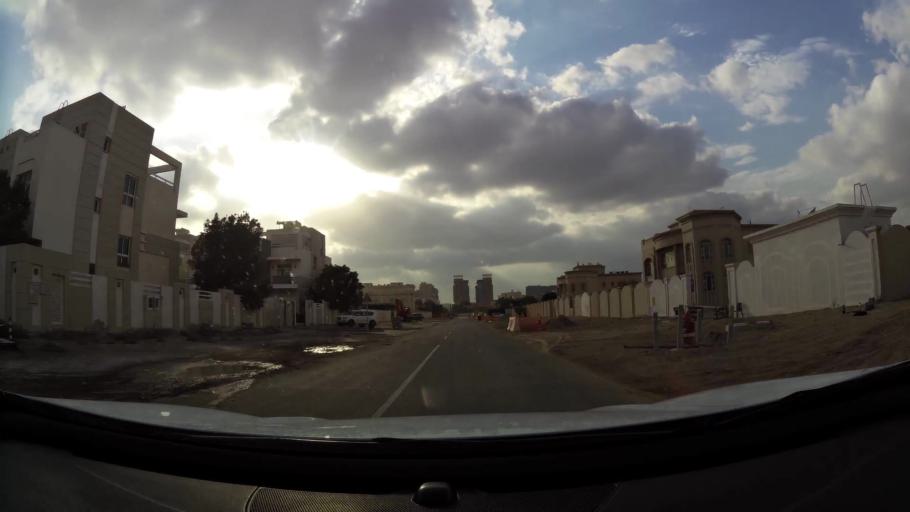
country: AE
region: Abu Dhabi
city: Abu Dhabi
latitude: 24.3733
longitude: 54.5452
